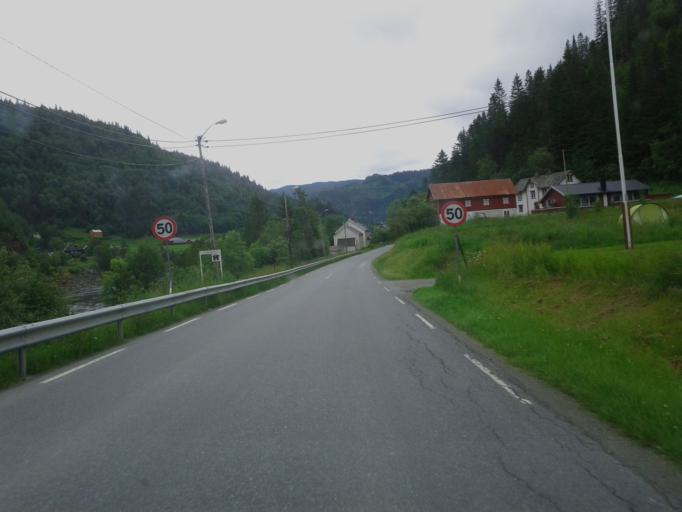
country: NO
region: Sor-Trondelag
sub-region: Midtre Gauldal
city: Storen
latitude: 63.0106
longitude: 10.4475
